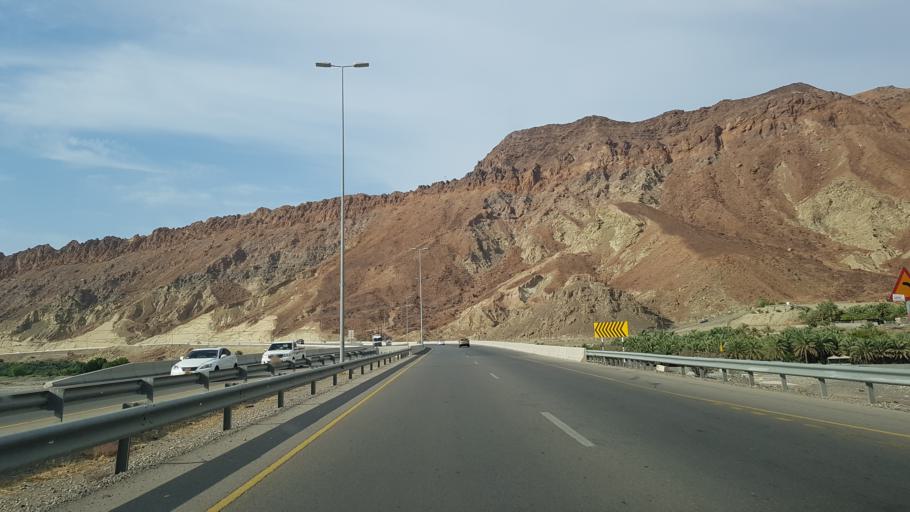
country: OM
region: Muhafazat ad Dakhiliyah
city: Bidbid
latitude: 23.4443
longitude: 58.1222
